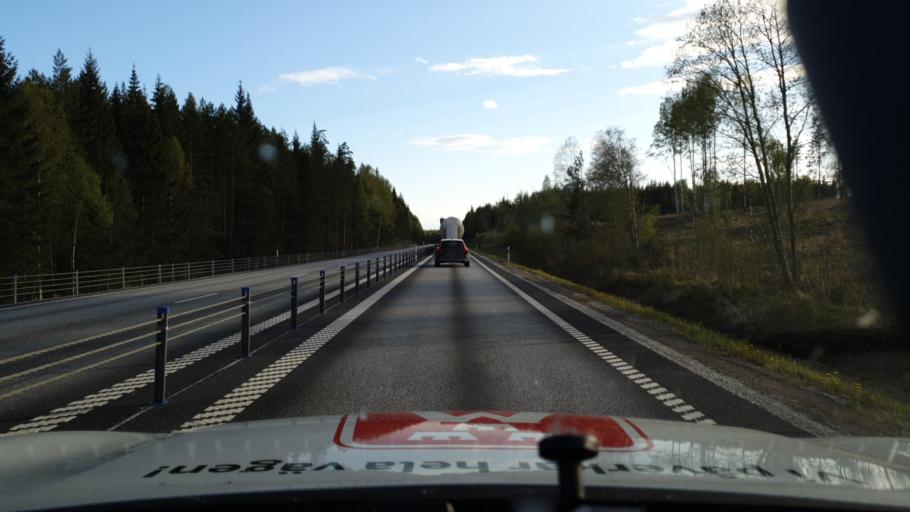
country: SE
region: Vaestmanland
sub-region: Fagersta Kommun
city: Fagersta
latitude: 60.0406
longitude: 15.8209
